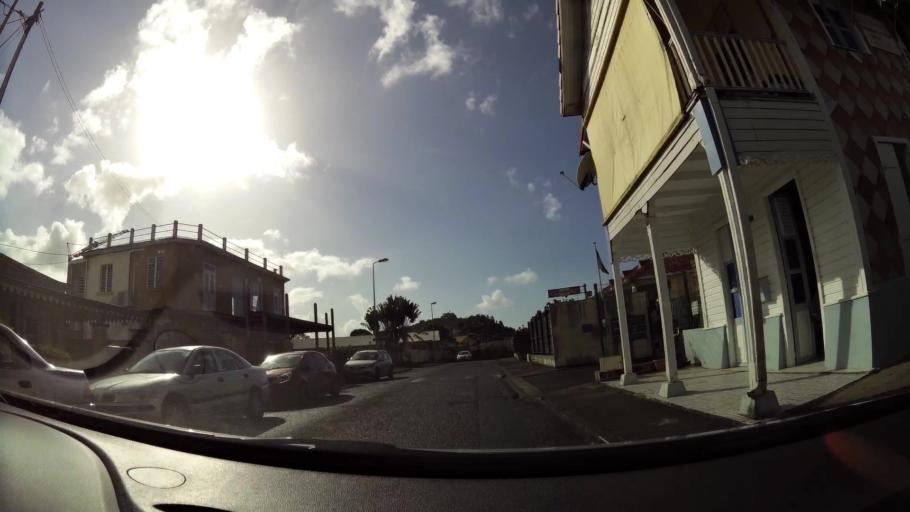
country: MQ
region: Martinique
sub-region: Martinique
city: Ducos
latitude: 14.5278
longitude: -60.9807
